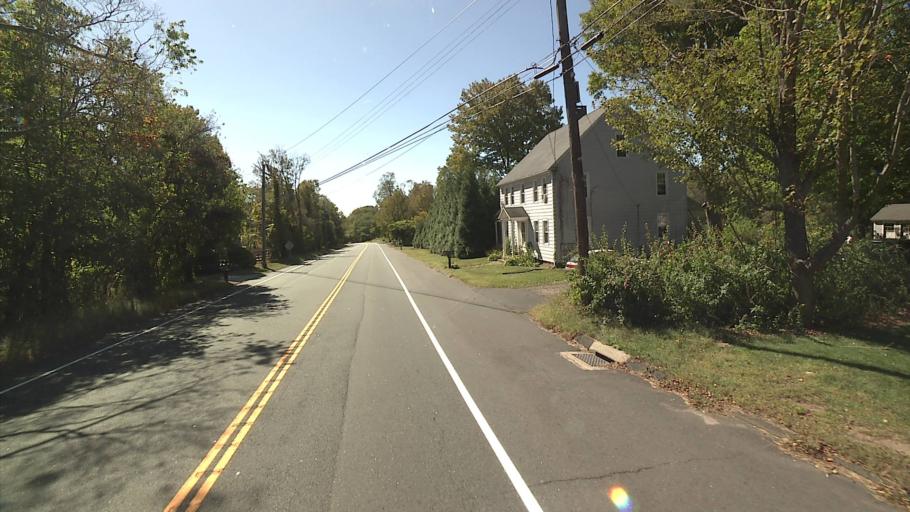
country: US
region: Connecticut
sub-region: New Haven County
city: Woodbridge
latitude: 41.3997
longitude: -72.9743
